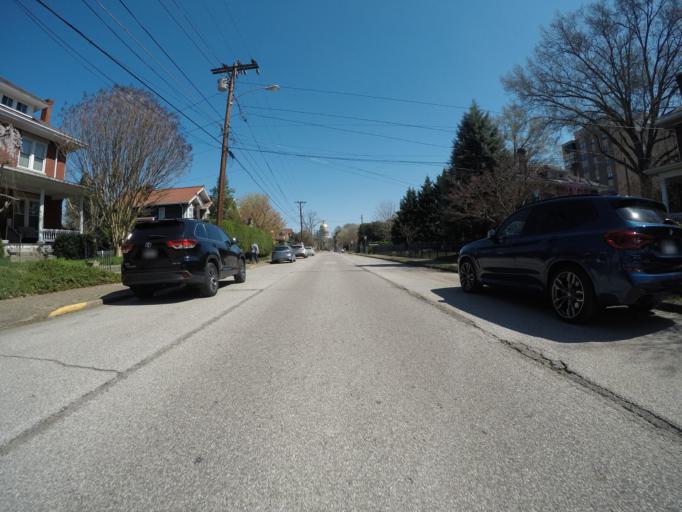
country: US
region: West Virginia
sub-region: Kanawha County
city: Charleston
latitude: 38.3394
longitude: -81.6206
